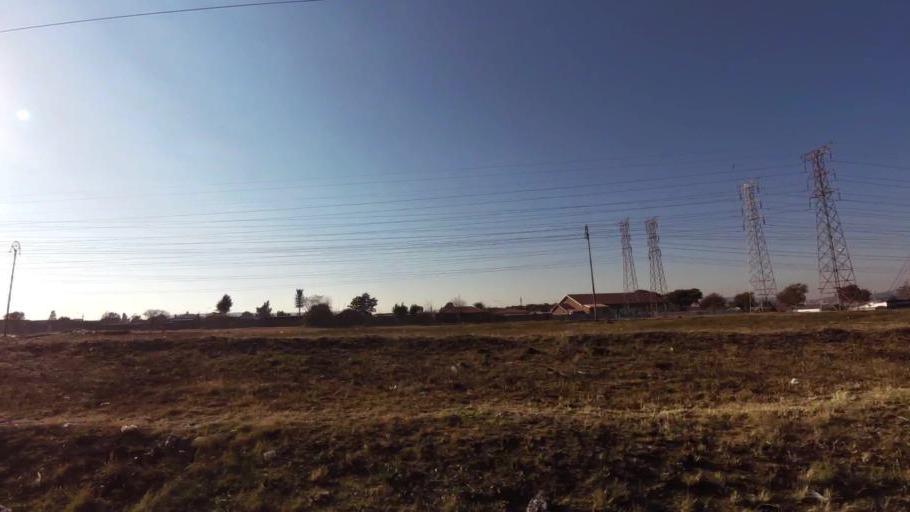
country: ZA
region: Gauteng
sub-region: City of Johannesburg Metropolitan Municipality
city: Soweto
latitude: -26.2422
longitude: 27.9356
